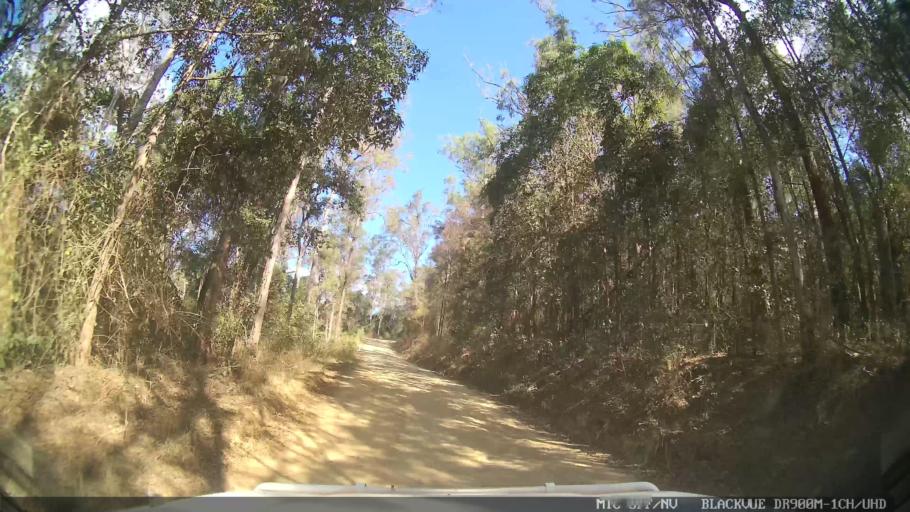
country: AU
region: Queensland
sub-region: Moreton Bay
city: Woodford
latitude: -26.6677
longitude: 152.6353
